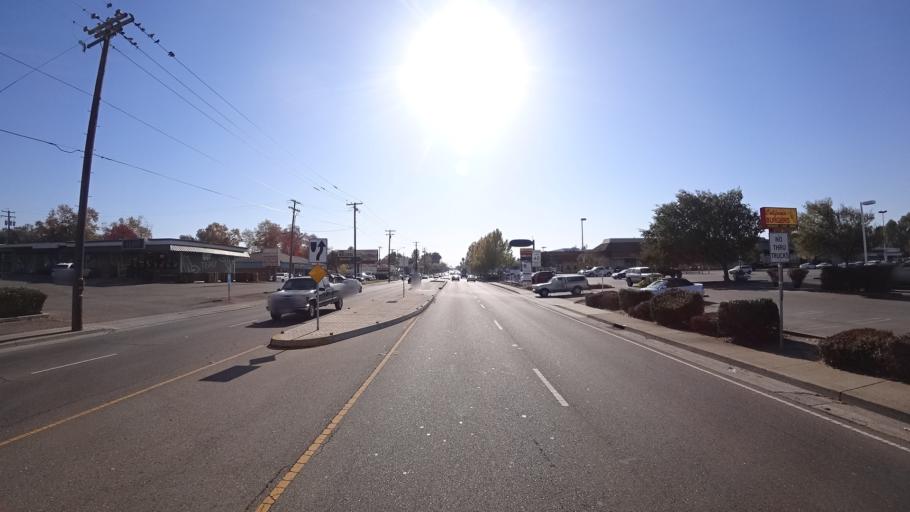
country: US
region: California
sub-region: Sacramento County
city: Citrus Heights
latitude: 38.7214
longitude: -121.2905
